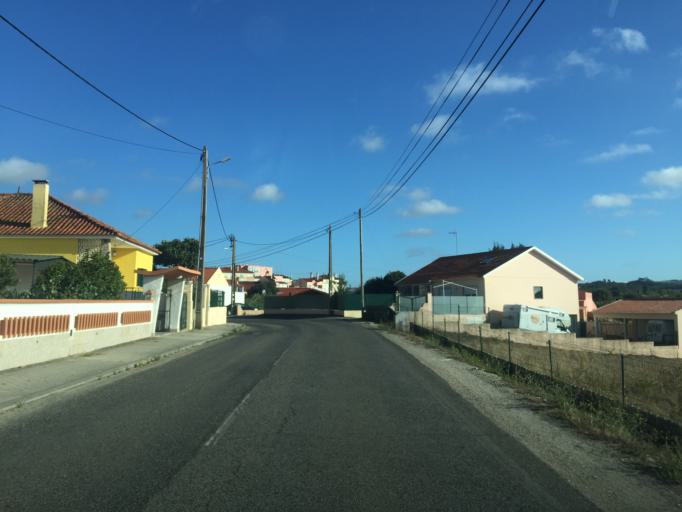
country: PT
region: Lisbon
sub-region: Torres Vedras
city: A dos Cunhados
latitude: 39.1552
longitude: -9.2996
